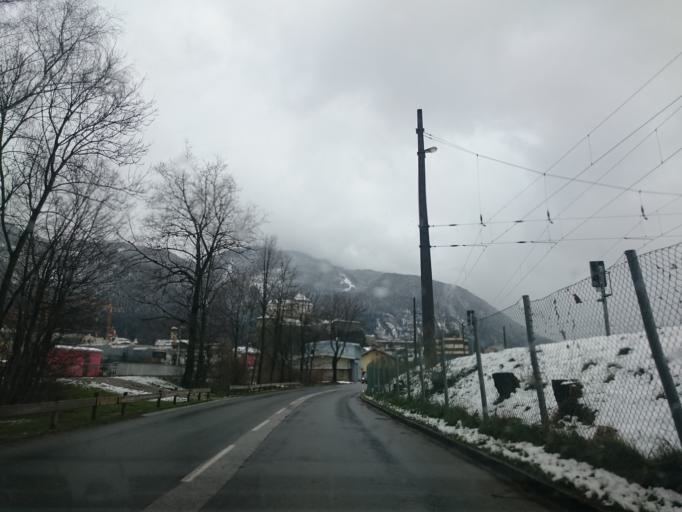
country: AT
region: Tyrol
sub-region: Politischer Bezirk Kufstein
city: Kufstein
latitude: 47.5867
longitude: 12.1658
